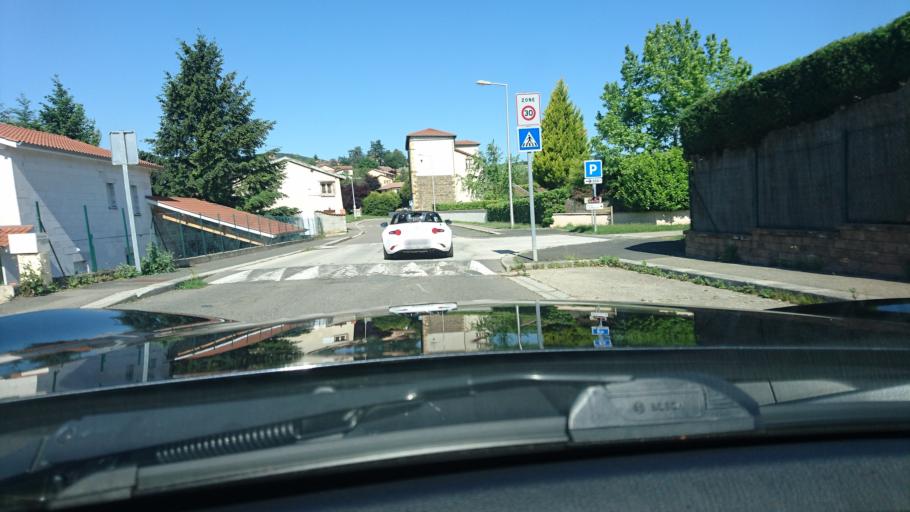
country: FR
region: Rhone-Alpes
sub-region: Departement du Rhone
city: Bessenay
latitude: 45.7763
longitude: 4.5501
